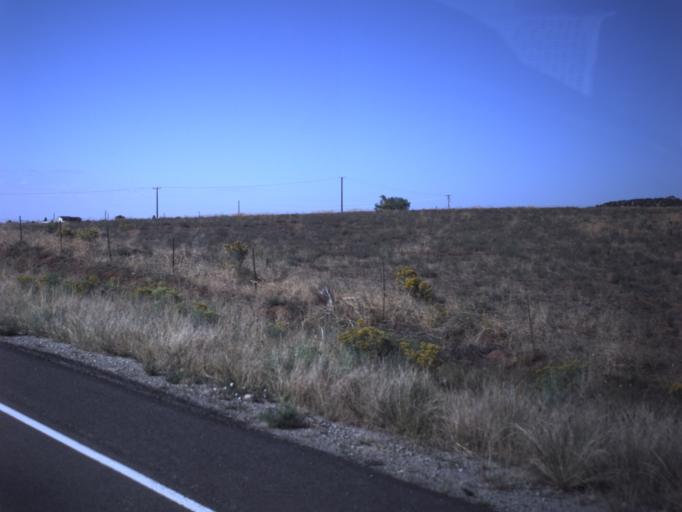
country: US
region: Utah
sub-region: San Juan County
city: Blanding
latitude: 37.6476
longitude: -109.4613
